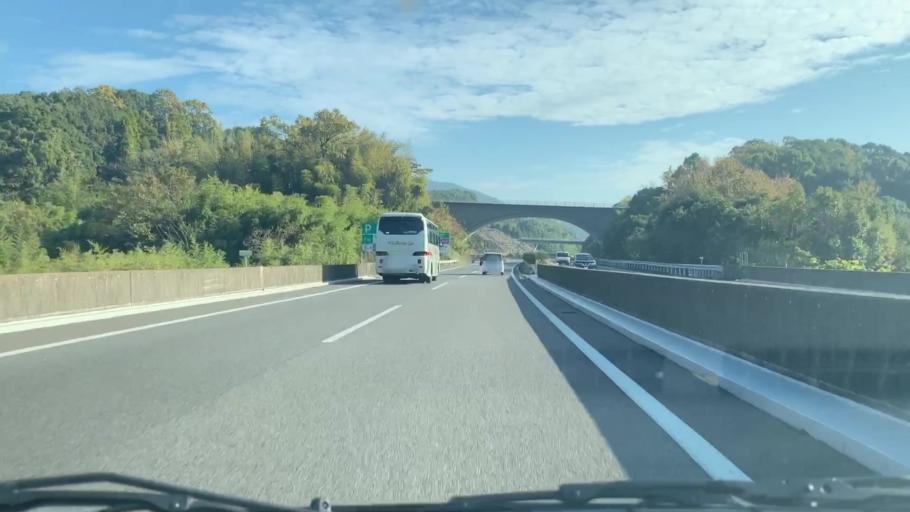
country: JP
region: Saga Prefecture
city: Saga-shi
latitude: 33.3083
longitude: 130.1984
